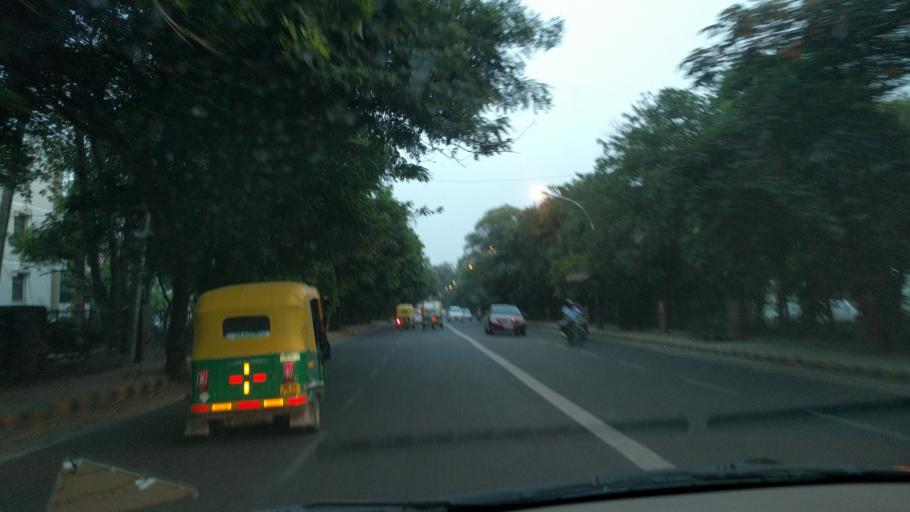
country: IN
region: Haryana
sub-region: Gurgaon
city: Gurgaon
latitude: 28.4516
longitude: 77.0615
